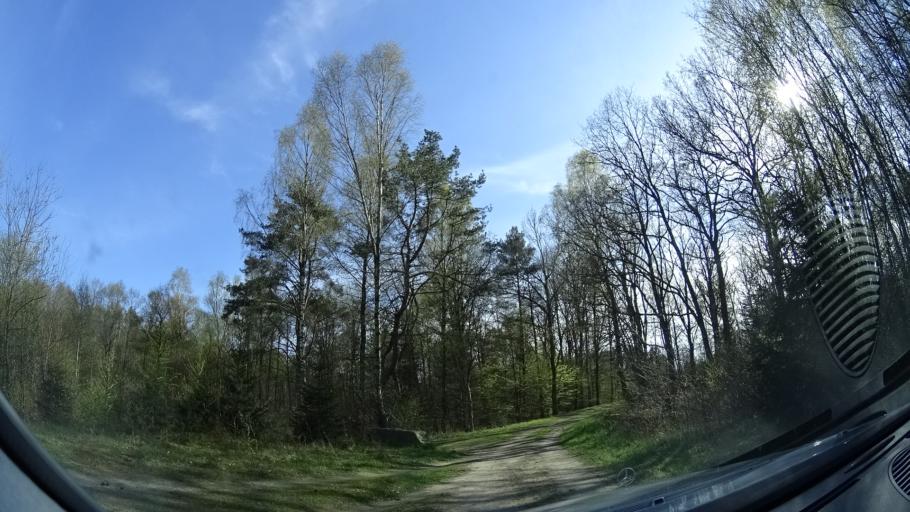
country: SE
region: Skane
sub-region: Hassleholms Kommun
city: Tormestorp
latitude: 56.0991
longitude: 13.6716
